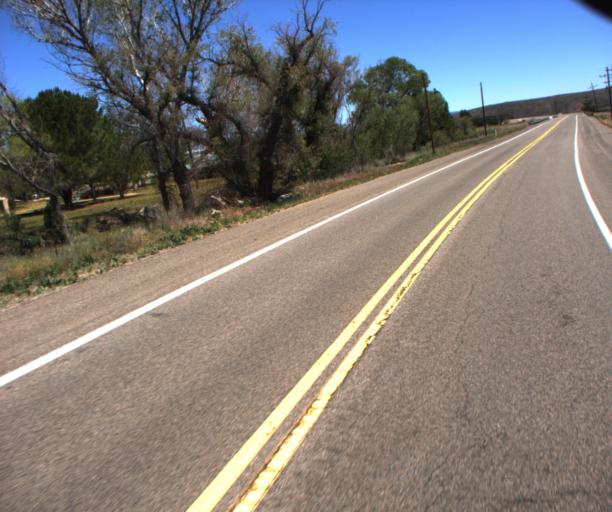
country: US
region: Arizona
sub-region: Yavapai County
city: Congress
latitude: 34.2762
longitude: -112.7265
